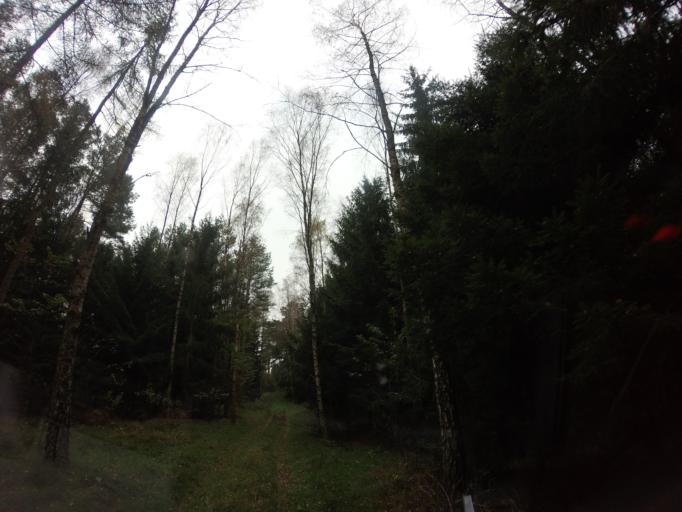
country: PL
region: West Pomeranian Voivodeship
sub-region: Powiat choszczenski
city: Bierzwnik
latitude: 53.1394
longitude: 15.6184
